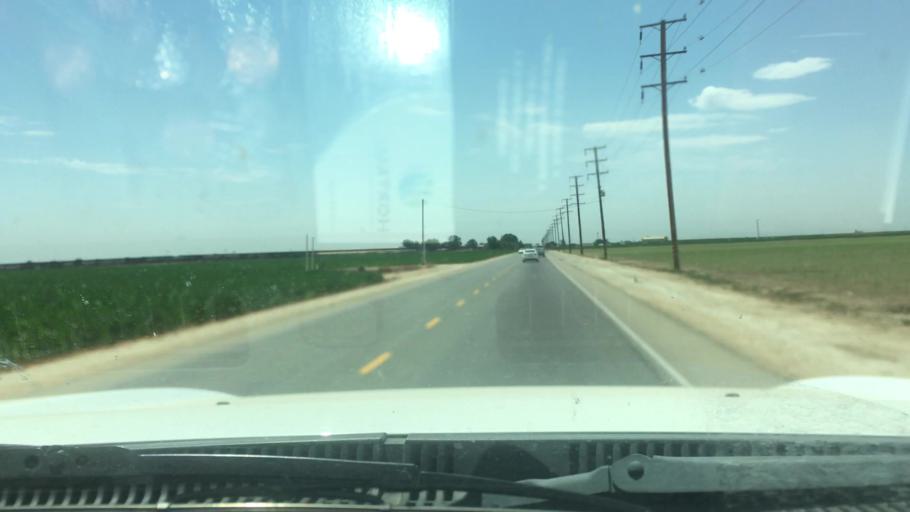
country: US
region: California
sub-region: Tulare County
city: Tipton
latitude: 36.0657
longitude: -119.2804
